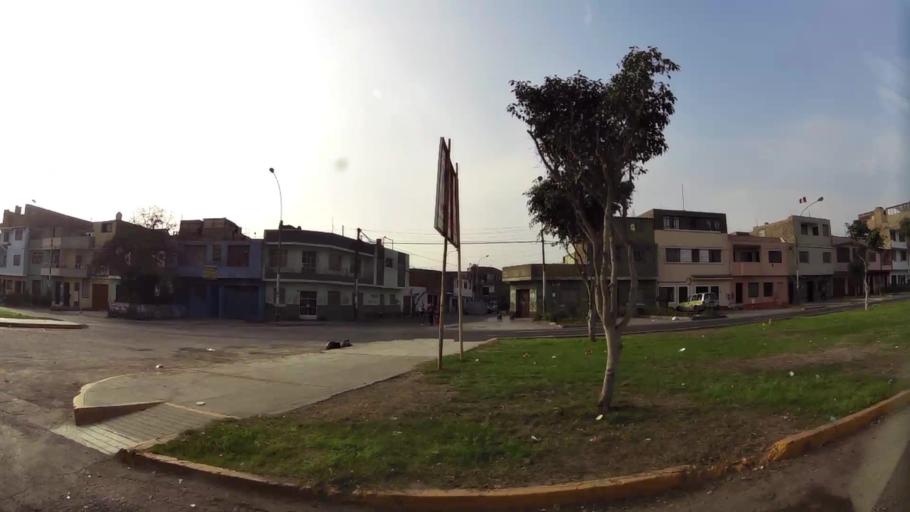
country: PE
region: Callao
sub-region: Callao
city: Callao
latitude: -12.0291
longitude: -77.0818
